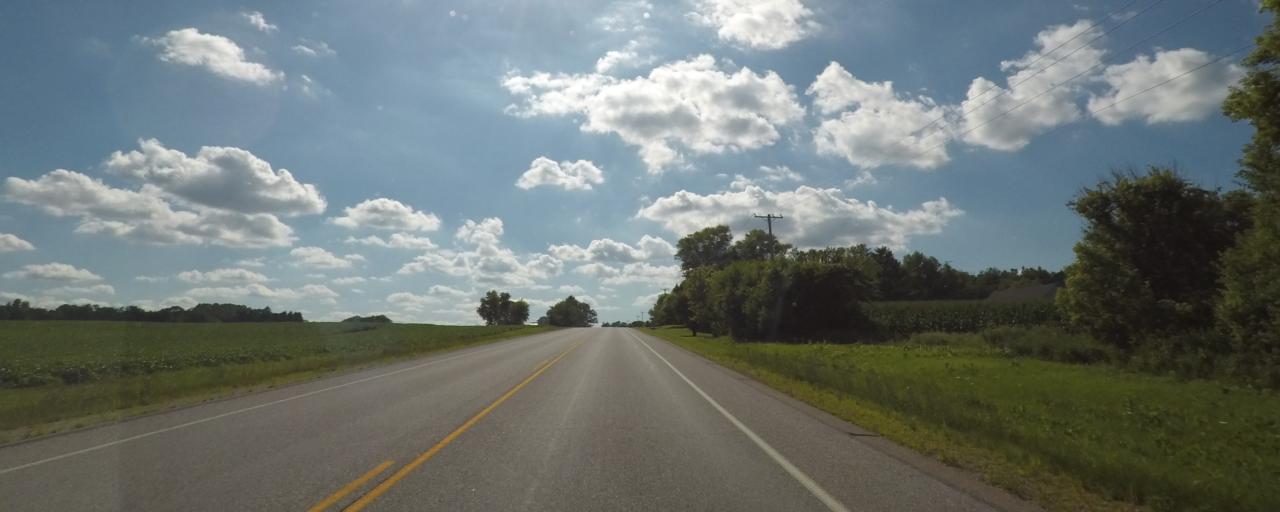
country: US
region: Wisconsin
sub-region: Dane County
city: Stoughton
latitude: 42.9198
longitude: -89.1247
